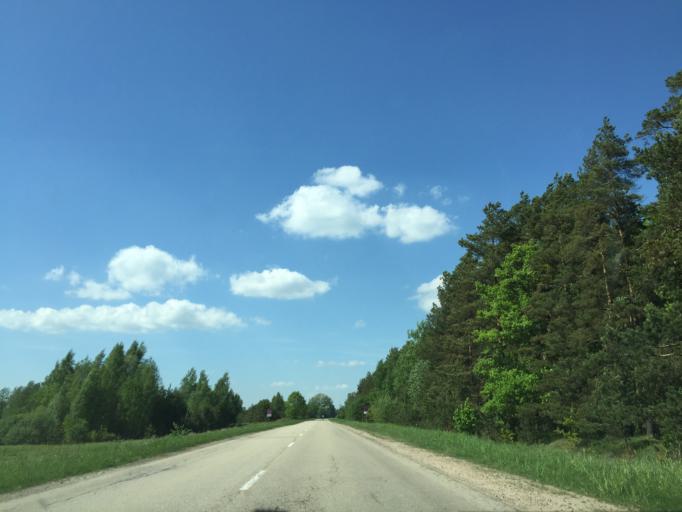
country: LV
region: Ozolnieku
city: Ozolnieki
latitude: 56.6134
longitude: 23.9393
